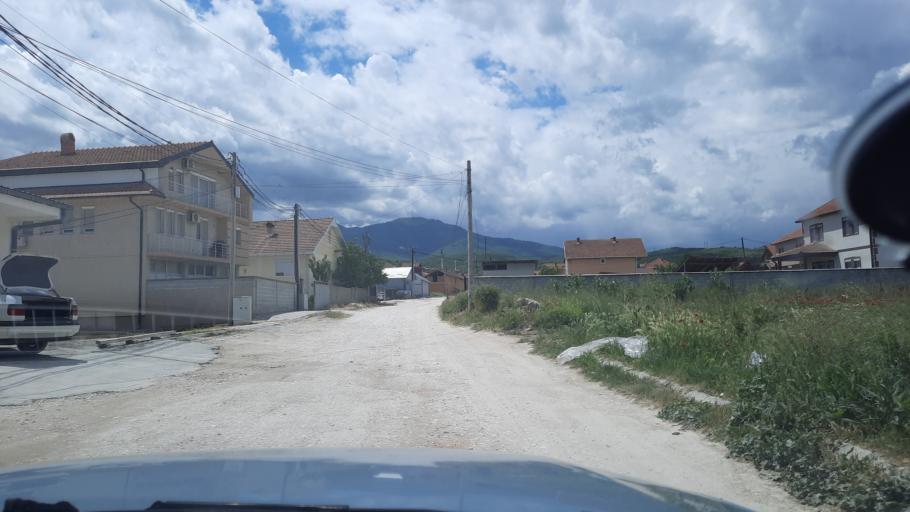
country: MK
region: Studenicani
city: Studenichani
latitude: 41.9265
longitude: 21.5402
